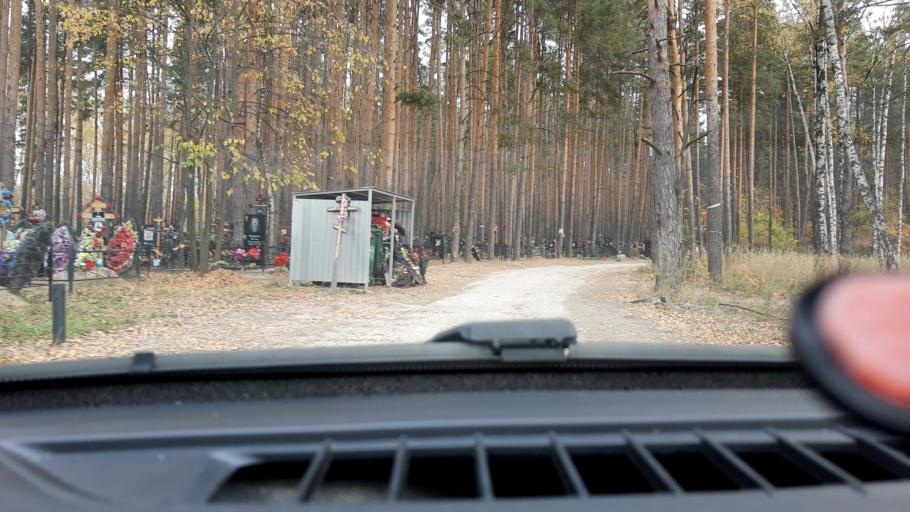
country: RU
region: Nizjnij Novgorod
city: Gorbatovka
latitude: 56.2864
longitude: 43.8217
